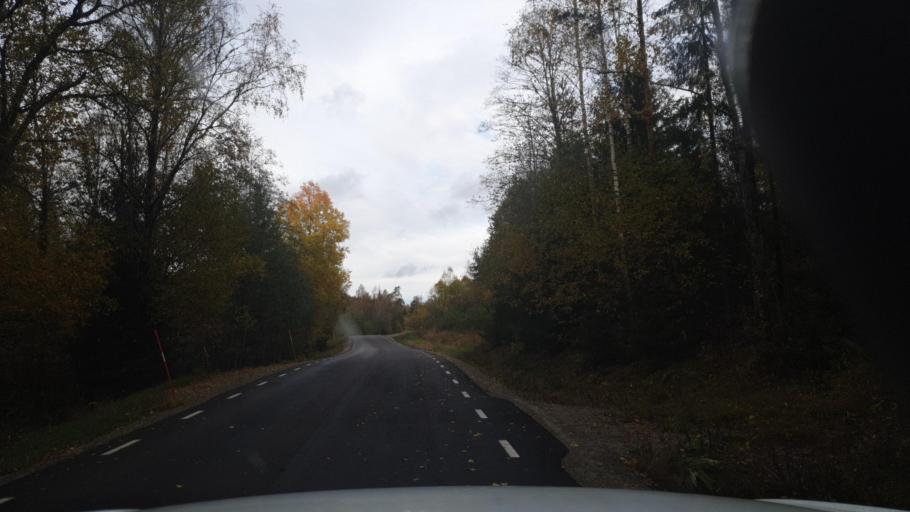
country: SE
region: Vaermland
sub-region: Sunne Kommun
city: Sunne
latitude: 59.6776
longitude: 12.8998
